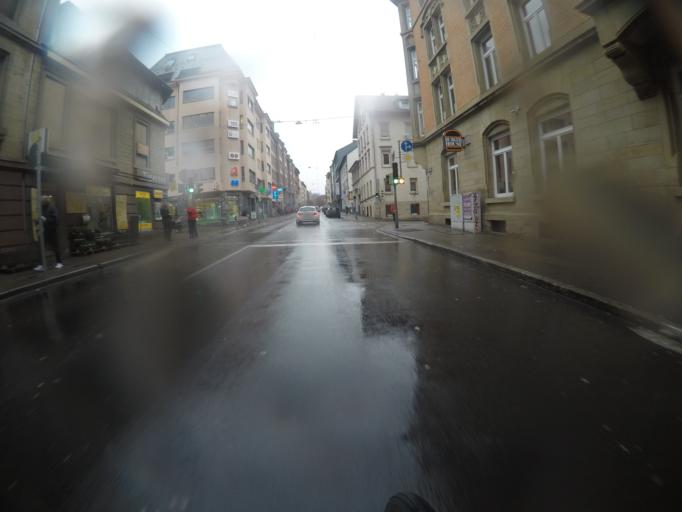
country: DE
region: Baden-Wuerttemberg
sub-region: Regierungsbezirk Stuttgart
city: Stuttgart
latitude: 48.7712
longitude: 9.1576
